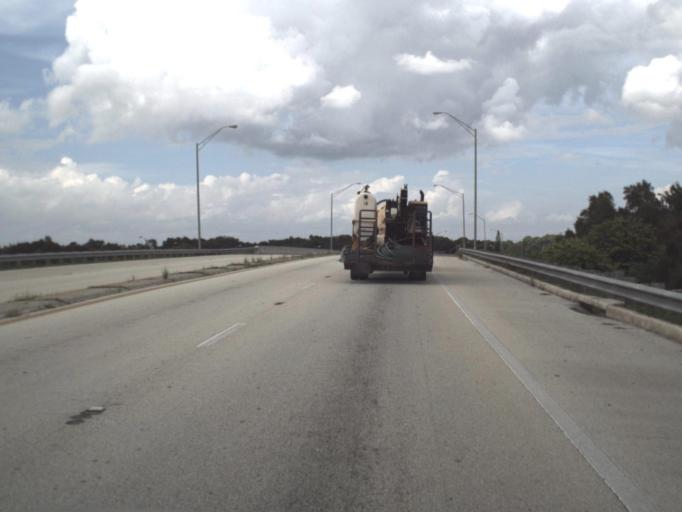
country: US
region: Florida
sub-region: Manatee County
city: Memphis
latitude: 27.5381
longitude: -82.5631
